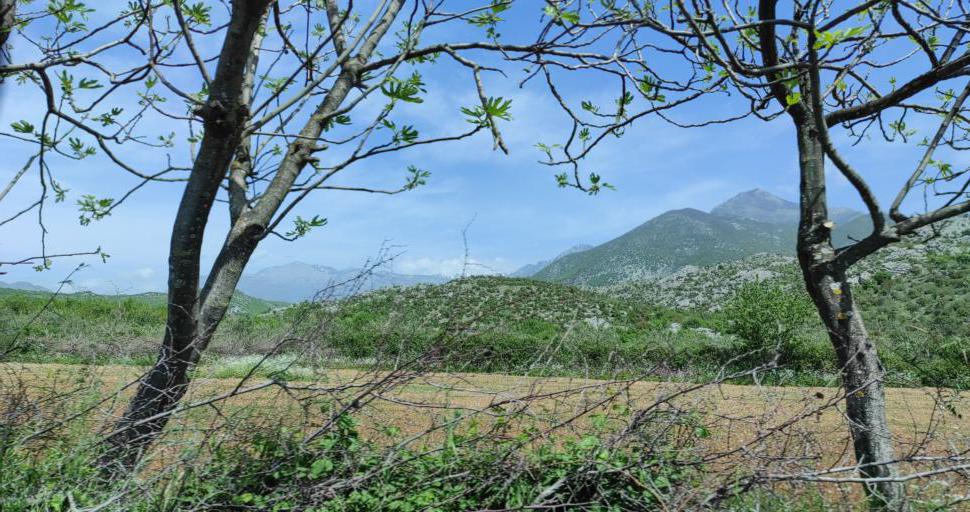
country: AL
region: Shkoder
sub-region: Rrethi i Malesia e Madhe
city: Gruemire
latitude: 42.1498
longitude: 19.5362
